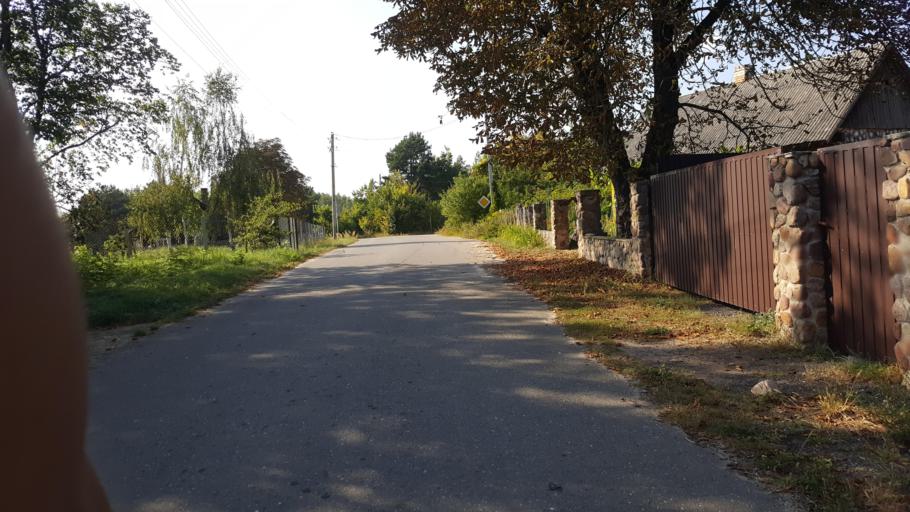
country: BY
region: Brest
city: Kamyanyuki
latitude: 52.5507
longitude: 23.6510
